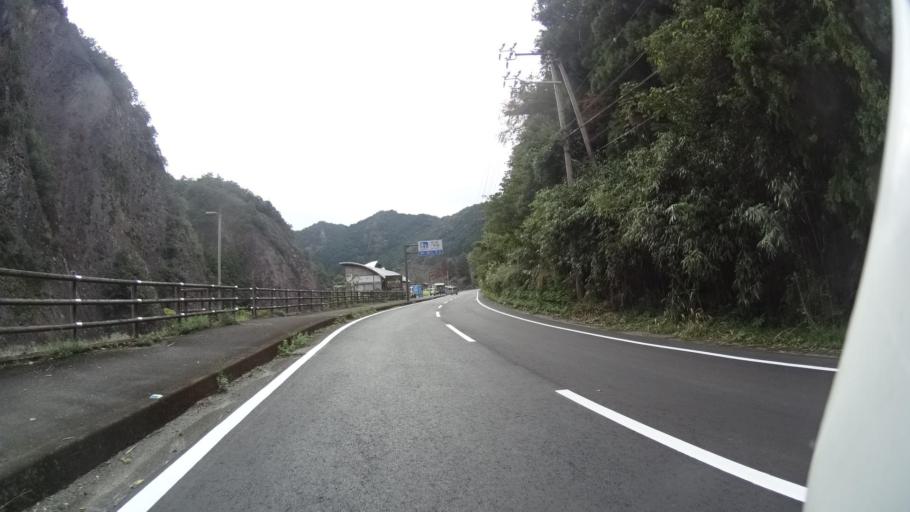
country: JP
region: Wakayama
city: Shingu
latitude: 33.5464
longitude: 135.7194
